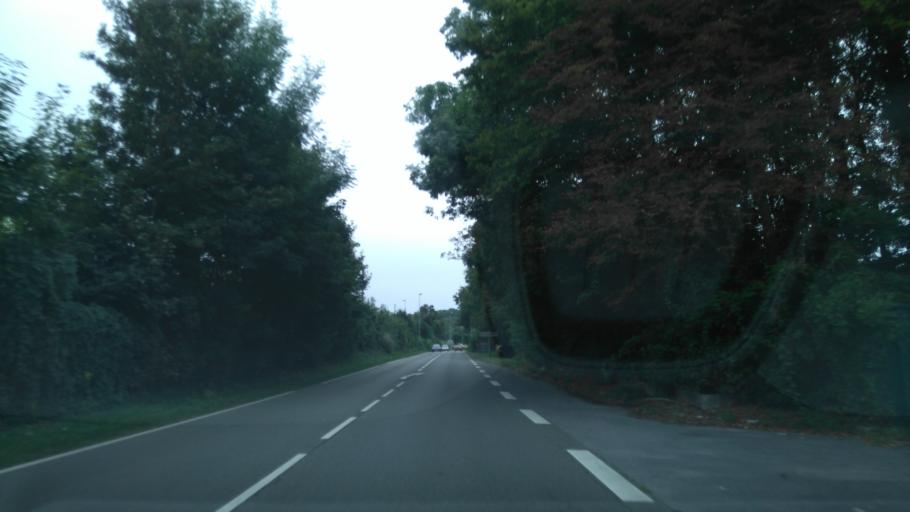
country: FR
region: Picardie
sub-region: Departement de l'Oise
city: Precy-sur-Oise
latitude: 49.2039
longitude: 2.3791
